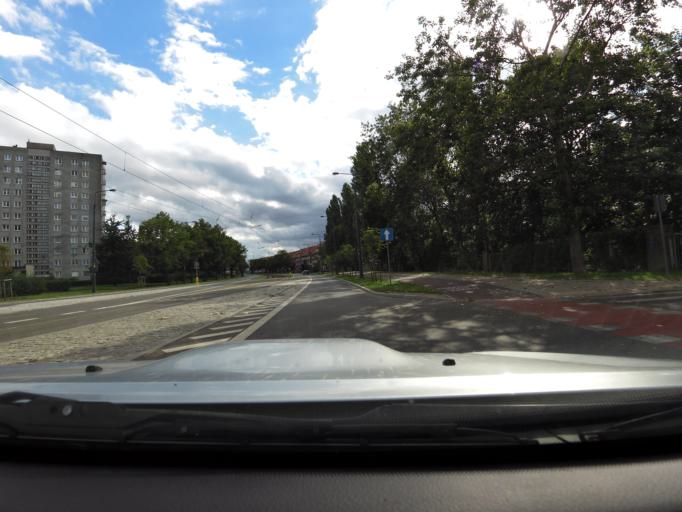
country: PL
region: Pomeranian Voivodeship
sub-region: Gdansk
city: Gdansk
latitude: 54.3521
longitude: 18.6713
